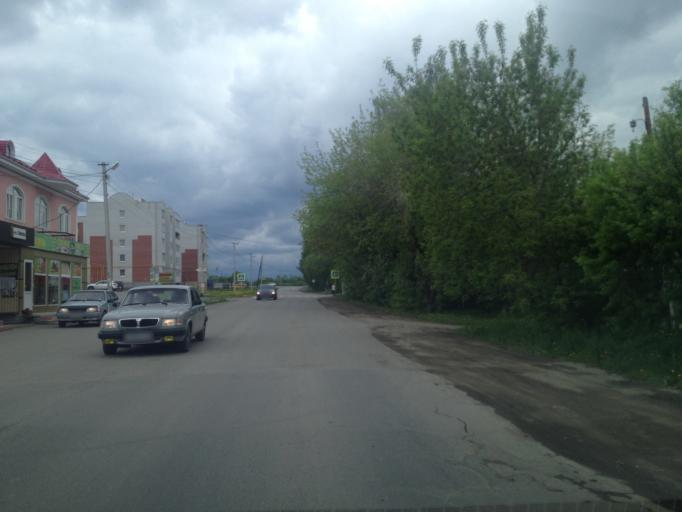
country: RU
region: Sverdlovsk
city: Aramil
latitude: 56.6851
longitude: 60.8416
